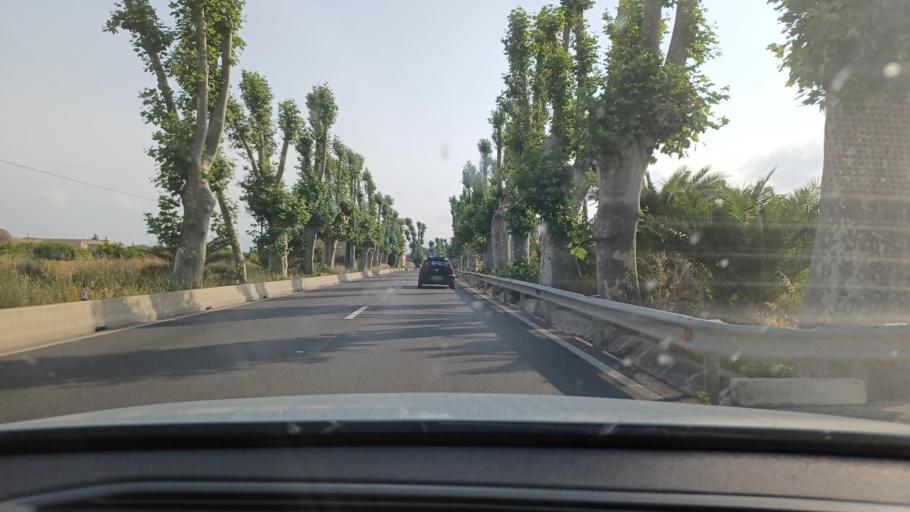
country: ES
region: Catalonia
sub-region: Provincia de Tarragona
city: Tortosa
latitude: 40.8011
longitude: 0.5018
